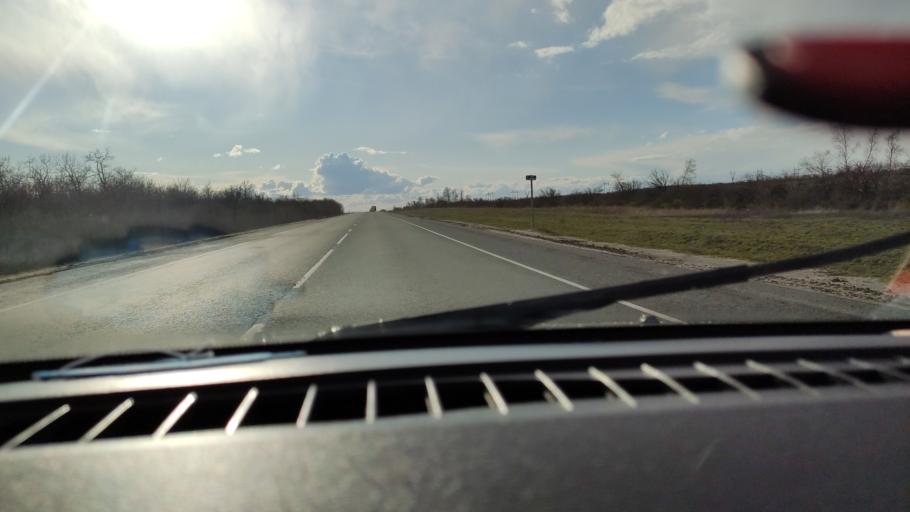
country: RU
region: Saratov
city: Yelshanka
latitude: 51.8212
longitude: 46.3380
